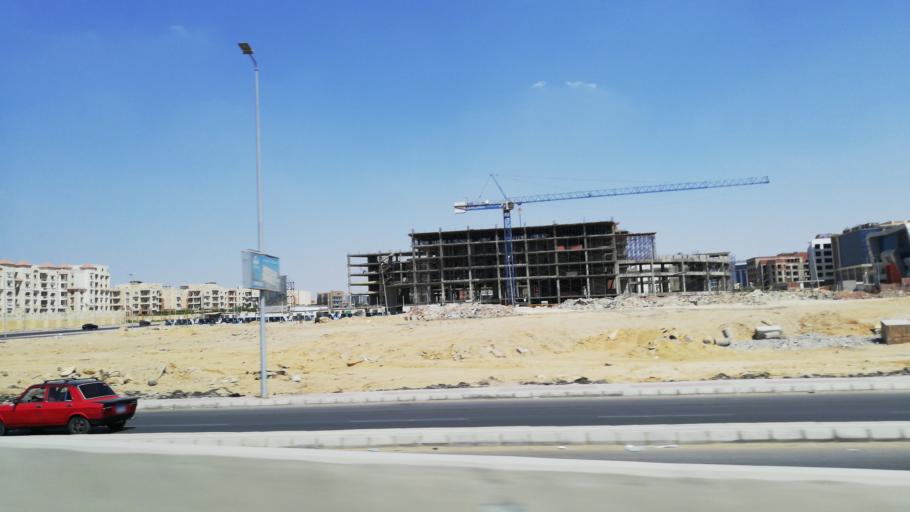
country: EG
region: Muhafazat al Qalyubiyah
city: Al Khankah
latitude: 30.0275
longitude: 31.4751
